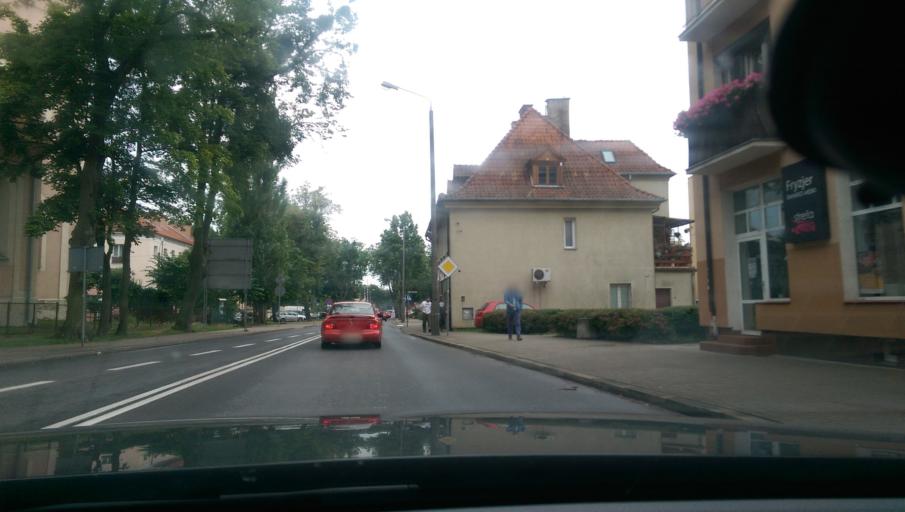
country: PL
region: Warmian-Masurian Voivodeship
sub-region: Powiat szczycienski
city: Szczytno
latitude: 53.5632
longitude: 20.9945
